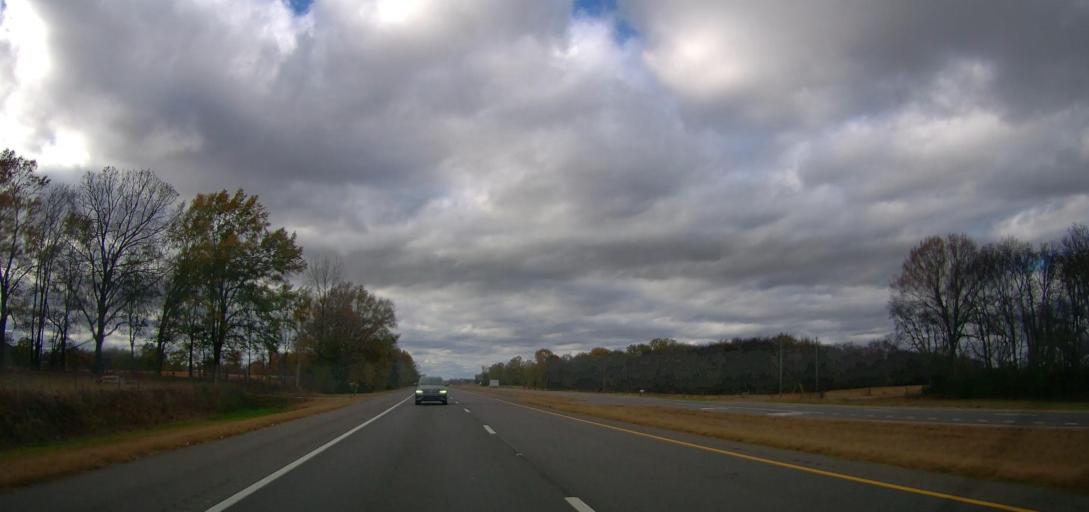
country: US
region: Alabama
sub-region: Lawrence County
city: Moulton
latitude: 34.4583
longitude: -87.2390
